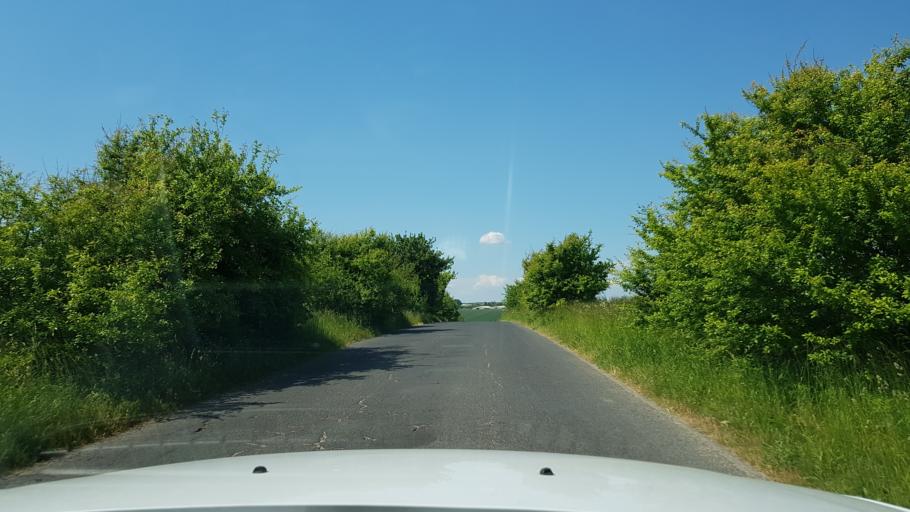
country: PL
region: West Pomeranian Voivodeship
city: Trzcinsko Zdroj
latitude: 53.0030
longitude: 14.5683
